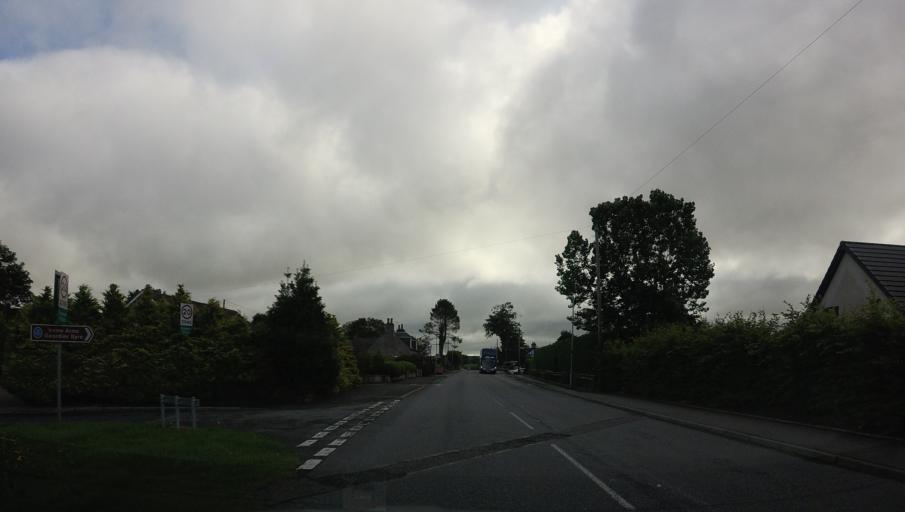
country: GB
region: Scotland
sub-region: Aberdeenshire
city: Westhill
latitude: 57.0795
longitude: -2.3462
